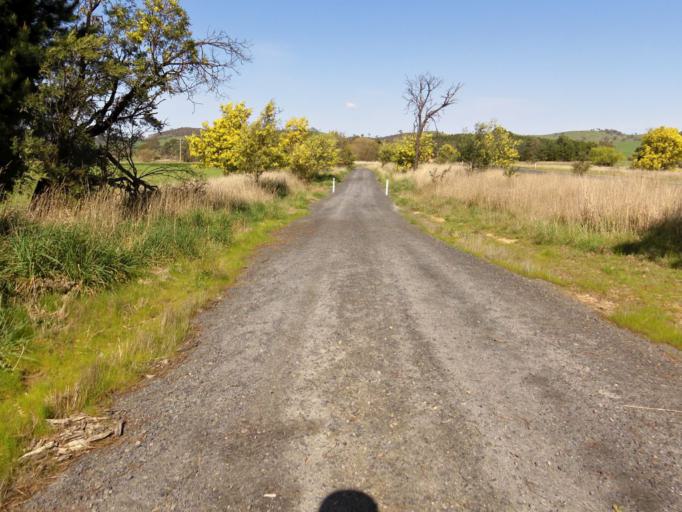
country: AU
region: Victoria
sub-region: Murrindindi
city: Alexandra
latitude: -37.0103
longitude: 145.7545
